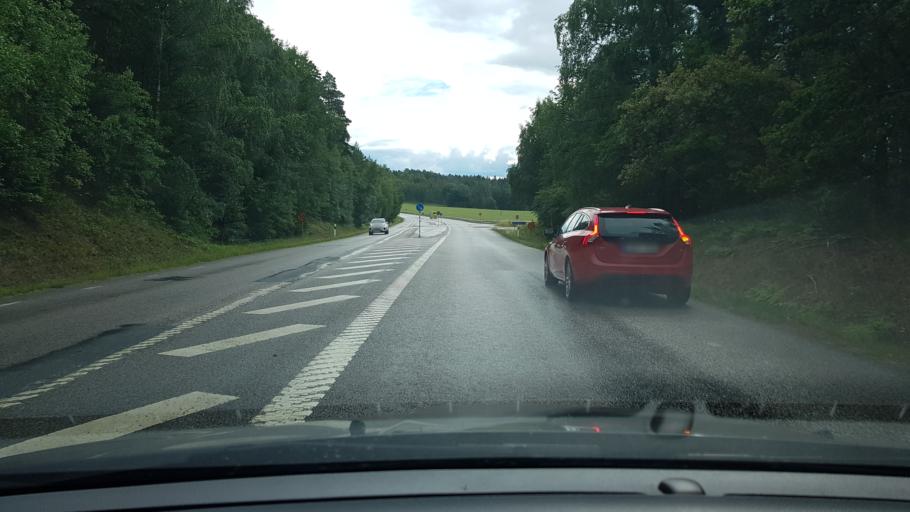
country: SE
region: Uppsala
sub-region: Uppsala Kommun
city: Saevja
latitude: 59.7861
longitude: 17.6670
